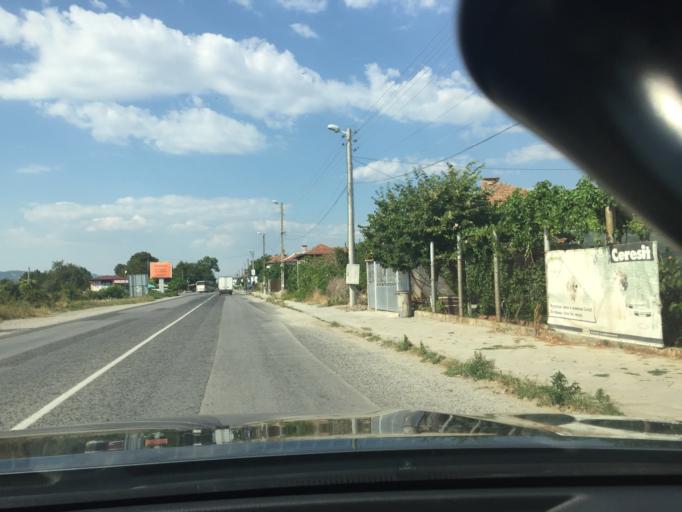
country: BG
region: Kyustendil
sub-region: Obshtina Kocherinovo
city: Kocherinovo
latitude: 42.1149
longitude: 23.0382
